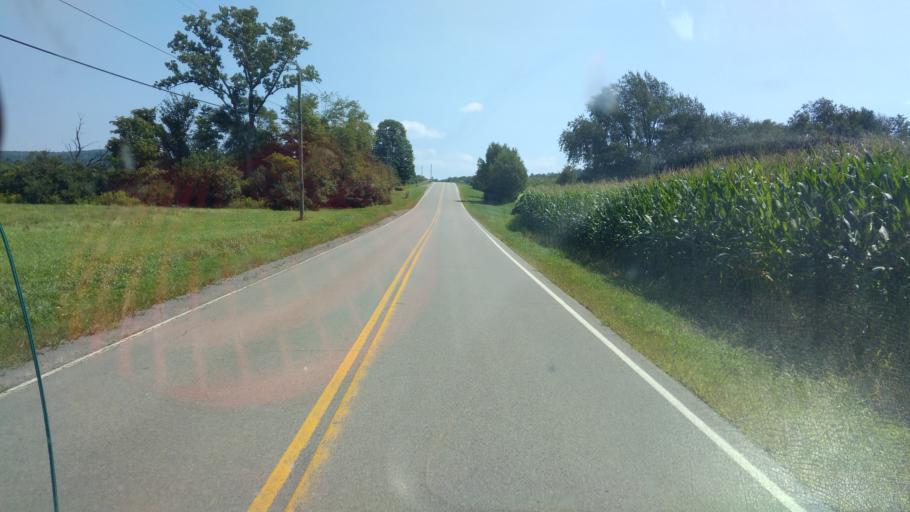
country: US
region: New York
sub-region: Allegany County
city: Belmont
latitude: 42.3005
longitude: -77.9639
